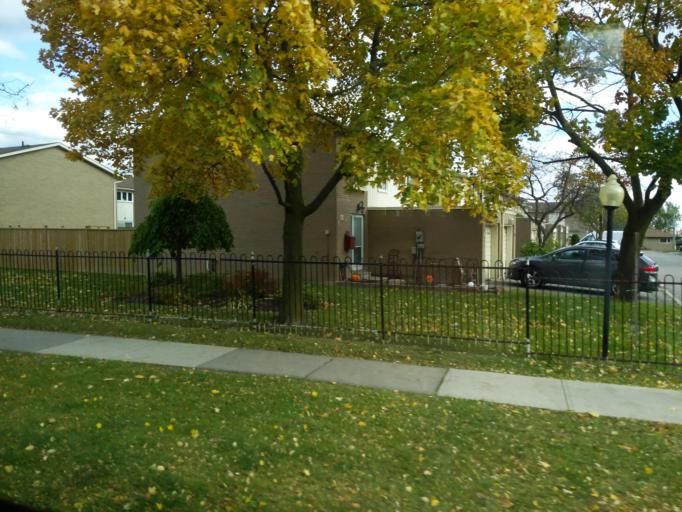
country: CA
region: Ontario
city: Brampton
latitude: 43.7182
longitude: -79.7133
